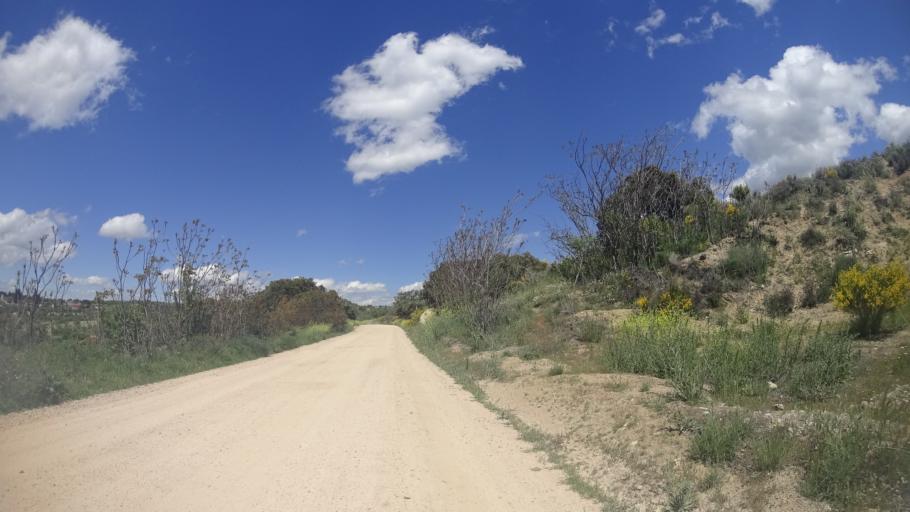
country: ES
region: Madrid
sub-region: Provincia de Madrid
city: San Martin de Valdeiglesias
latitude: 40.3640
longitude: -4.3858
